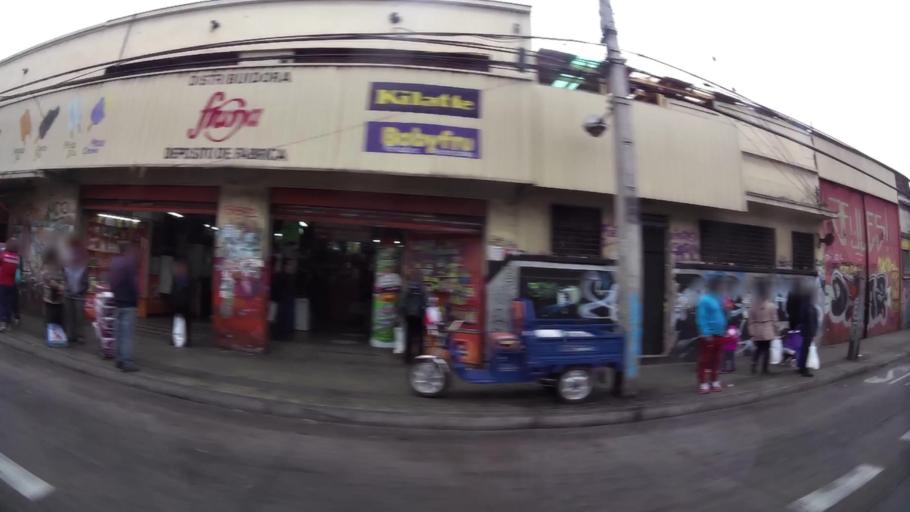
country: CL
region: Santiago Metropolitan
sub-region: Provincia de Santiago
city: Santiago
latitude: -33.4727
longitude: -70.6439
